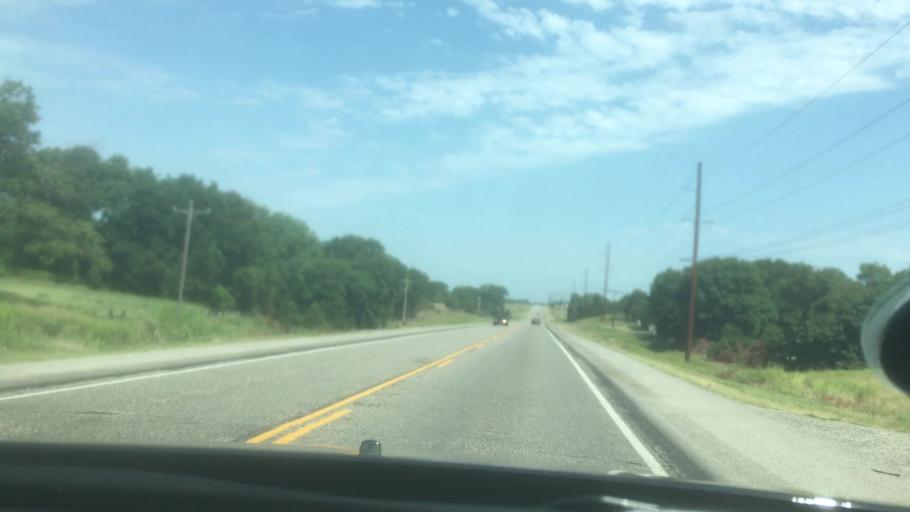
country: US
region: Oklahoma
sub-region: Seminole County
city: Konawa
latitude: 34.8427
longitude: -96.7997
